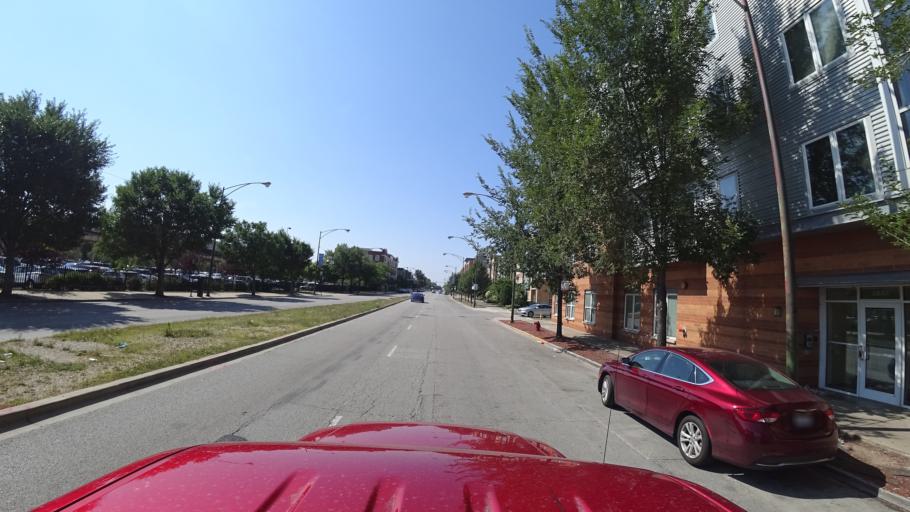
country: US
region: Illinois
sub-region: Cook County
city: Chicago
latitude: 41.8304
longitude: -87.6266
